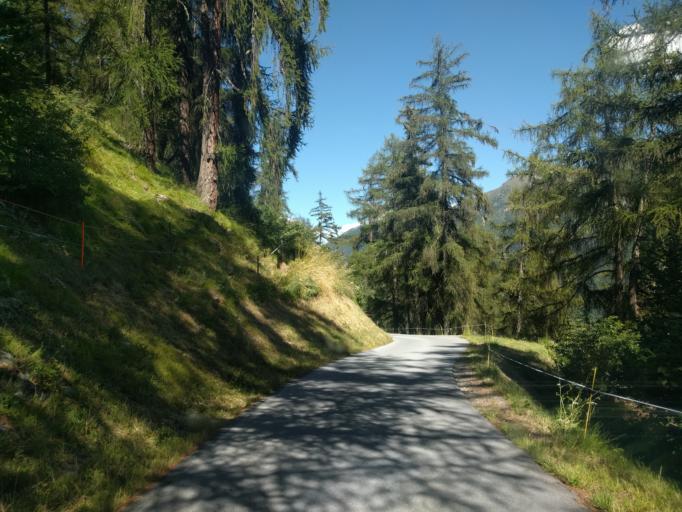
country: IT
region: Trentino-Alto Adige
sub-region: Bolzano
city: Tubre
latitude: 46.6072
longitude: 10.4141
